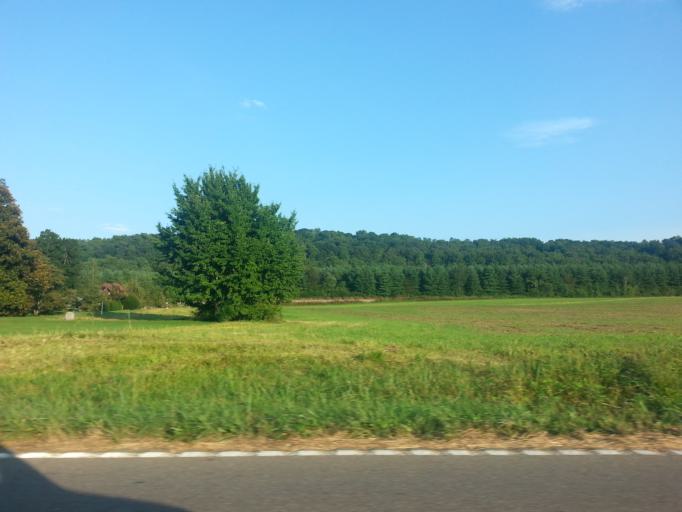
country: US
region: Tennessee
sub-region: McMinn County
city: Athens
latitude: 35.5058
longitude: -84.5629
